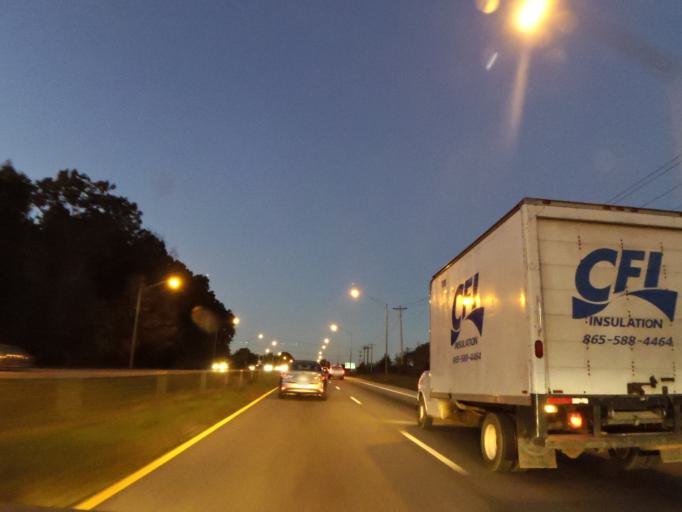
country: US
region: Tennessee
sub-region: Blount County
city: Alcoa
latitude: 35.7955
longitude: -83.9918
